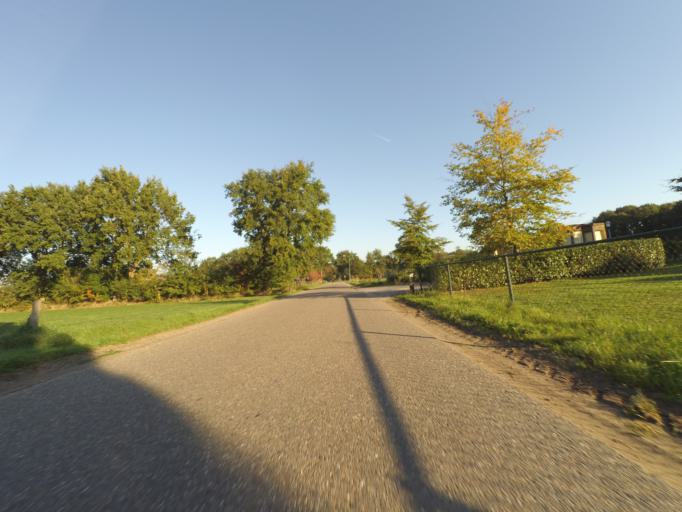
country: NL
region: Gelderland
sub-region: Gemeente Barneveld
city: Zwartebroek
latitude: 52.2027
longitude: 5.5426
